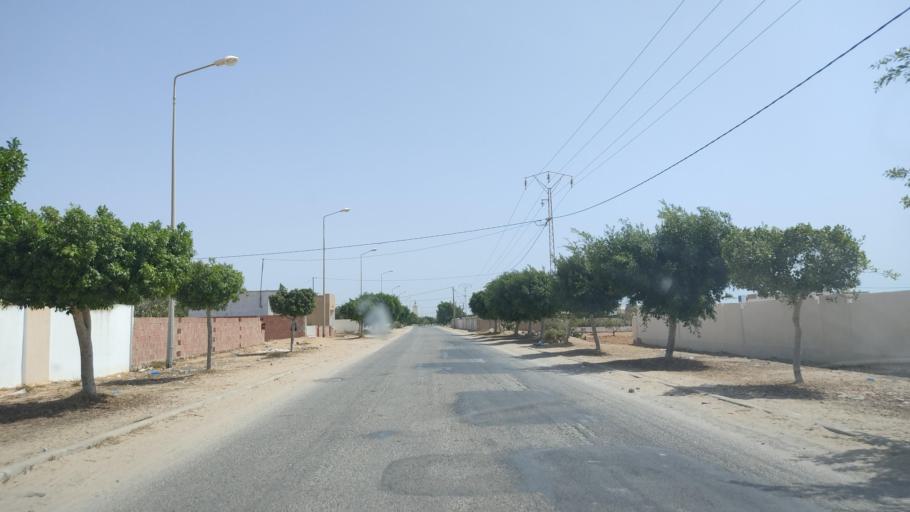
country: TN
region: Safaqis
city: Sfax
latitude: 34.6684
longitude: 10.7117
